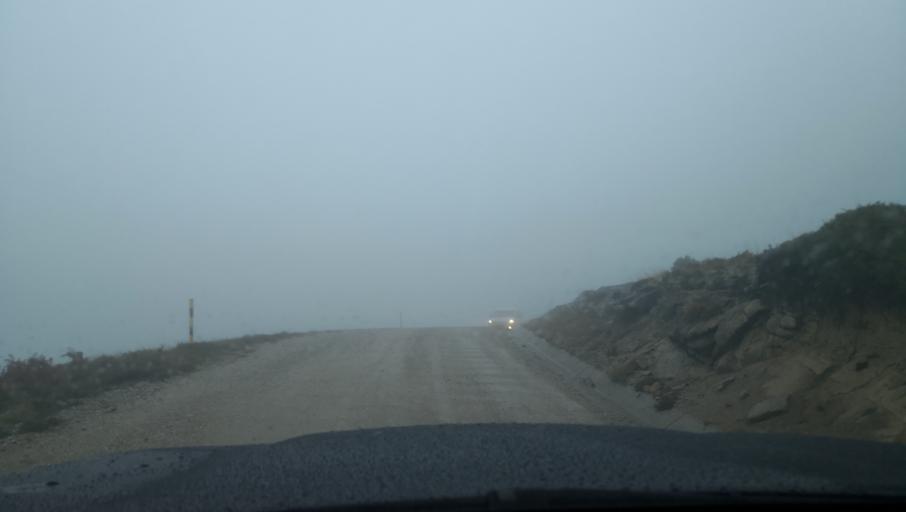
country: PT
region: Vila Real
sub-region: Vila Real
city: Vila Real
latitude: 41.3341
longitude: -7.8368
